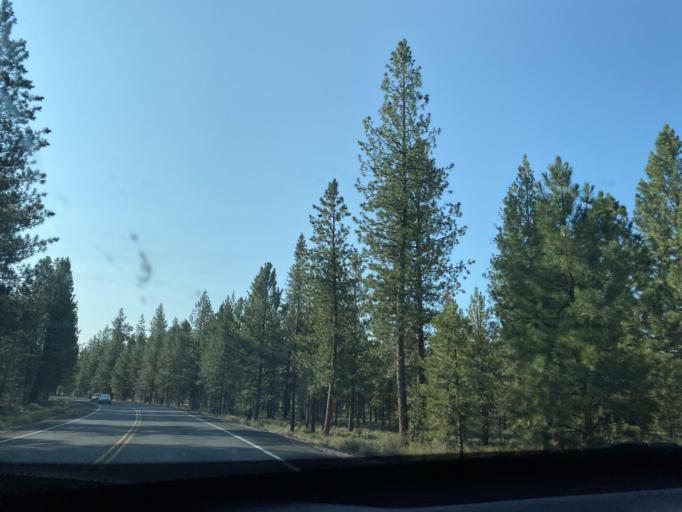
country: US
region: Oregon
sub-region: Deschutes County
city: La Pine
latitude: 43.7122
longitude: -121.4112
